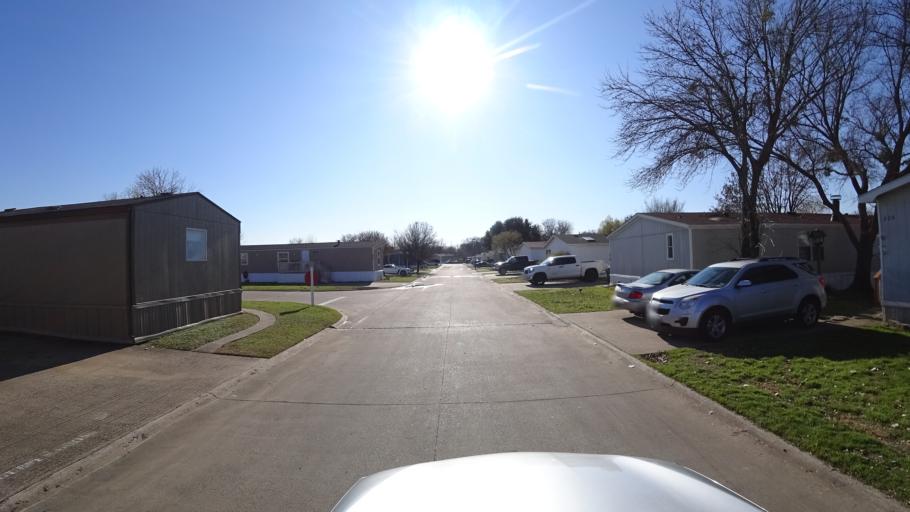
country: US
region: Texas
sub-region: Dallas County
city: Coppell
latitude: 32.9923
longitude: -97.0192
